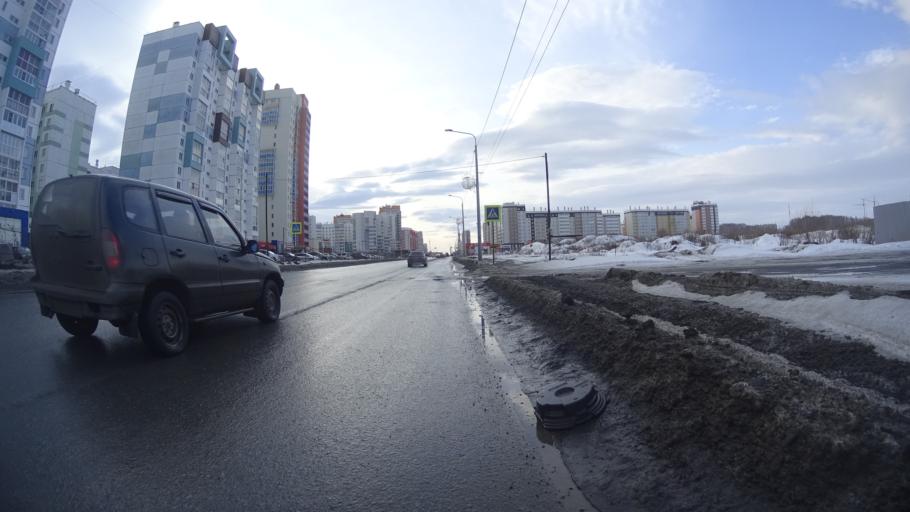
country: RU
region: Chelyabinsk
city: Roshchino
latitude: 55.2091
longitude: 61.2966
